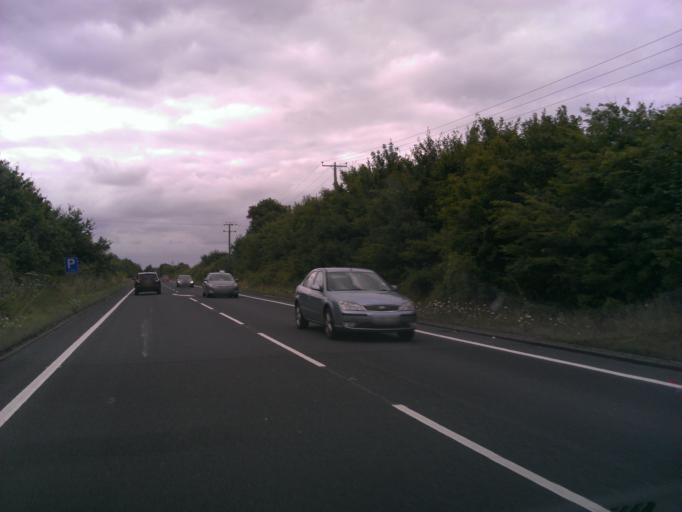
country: GB
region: England
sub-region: Essex
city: Little Clacton
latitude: 51.8247
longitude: 1.1331
